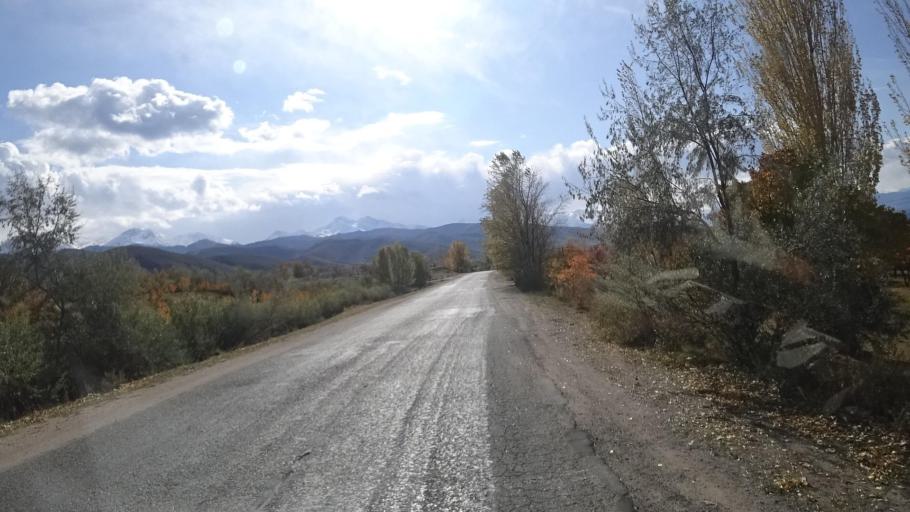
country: KG
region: Ysyk-Koel
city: Pokrovka
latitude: 42.2283
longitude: 77.7144
